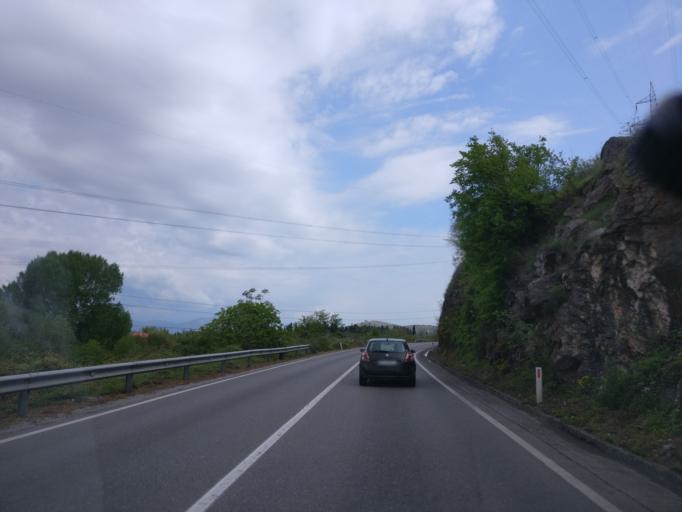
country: ME
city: Spuz
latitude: 42.4491
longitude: 19.2004
